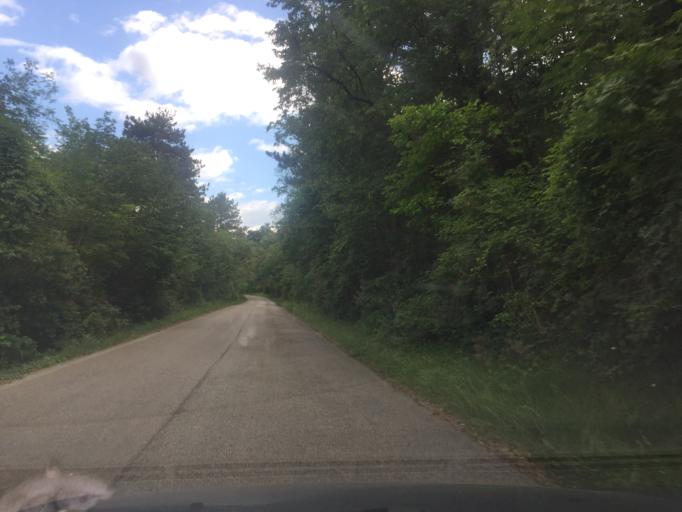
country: IT
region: Friuli Venezia Giulia
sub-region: Provincia di Gorizia
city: Savogna d'Isonzo
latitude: 45.8901
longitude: 13.5635
